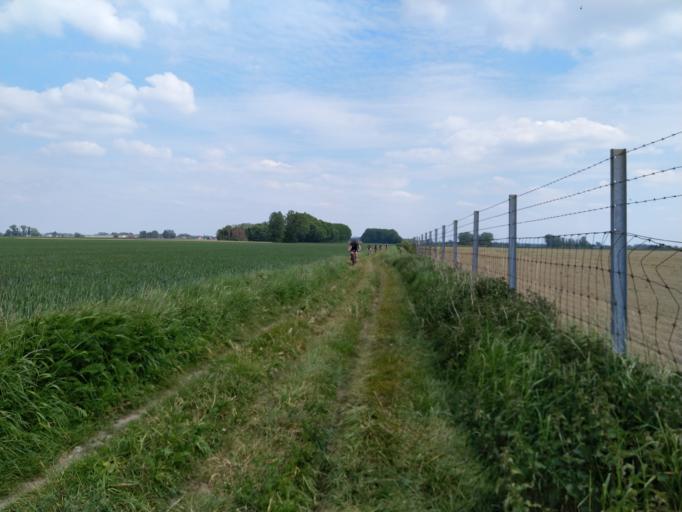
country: BE
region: Wallonia
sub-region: Province du Hainaut
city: Jurbise
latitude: 50.5479
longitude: 3.9327
